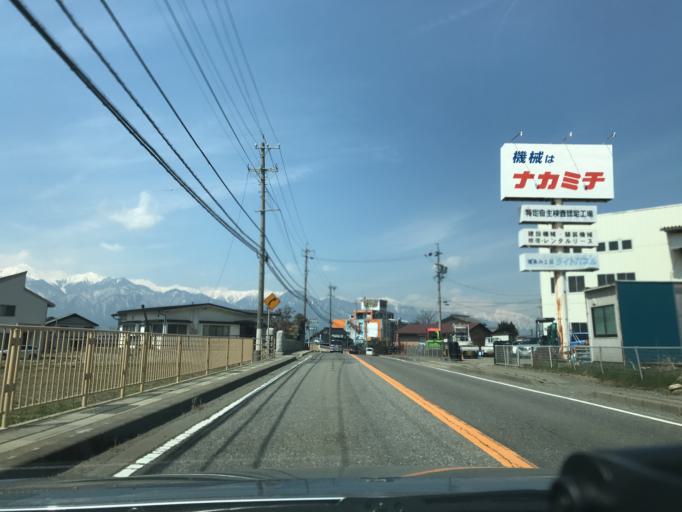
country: JP
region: Nagano
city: Toyoshina
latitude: 36.3075
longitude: 137.9381
